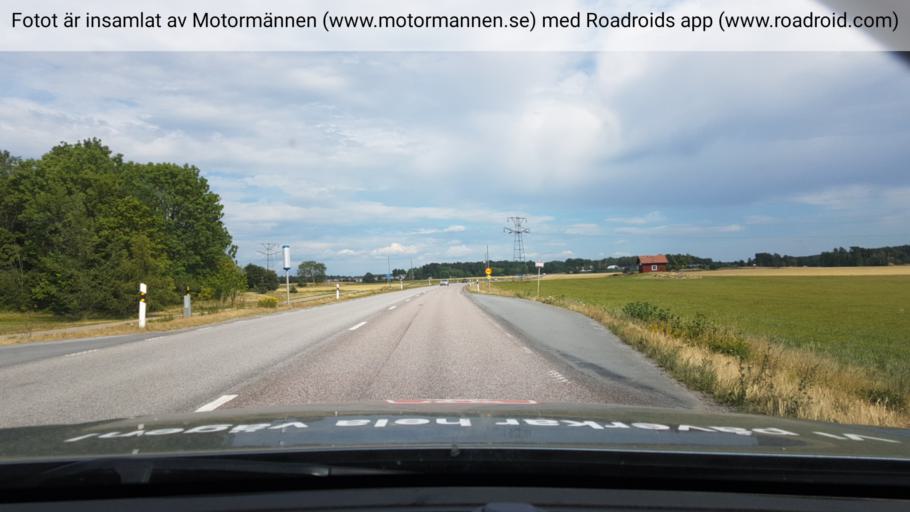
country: SE
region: Uppsala
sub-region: Uppsala Kommun
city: Uppsala
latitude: 59.8489
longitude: 17.5318
